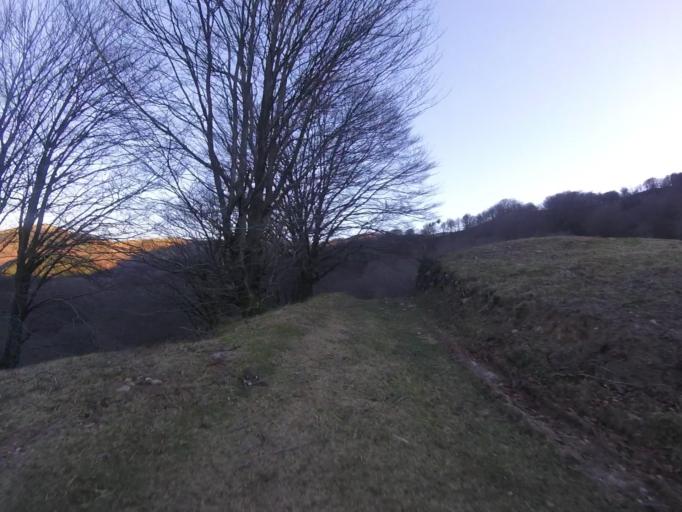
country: ES
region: Basque Country
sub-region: Provincia de Guipuzcoa
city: Irun
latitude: 43.2594
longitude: -1.8235
